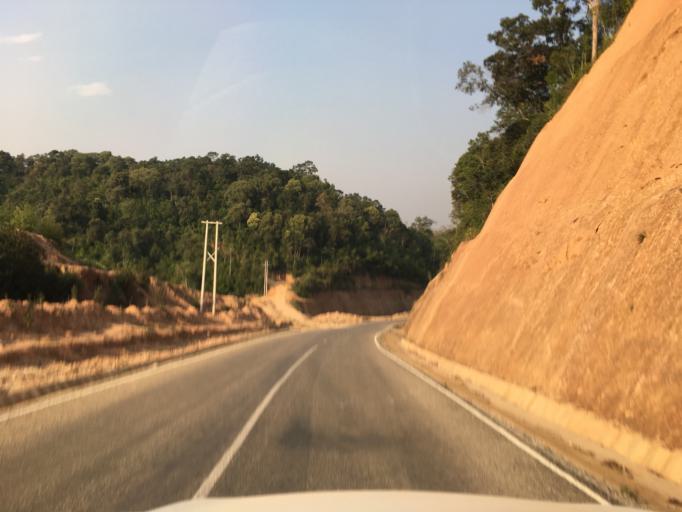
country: LA
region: Houaphan
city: Xam Nua
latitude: 20.5888
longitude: 104.0627
